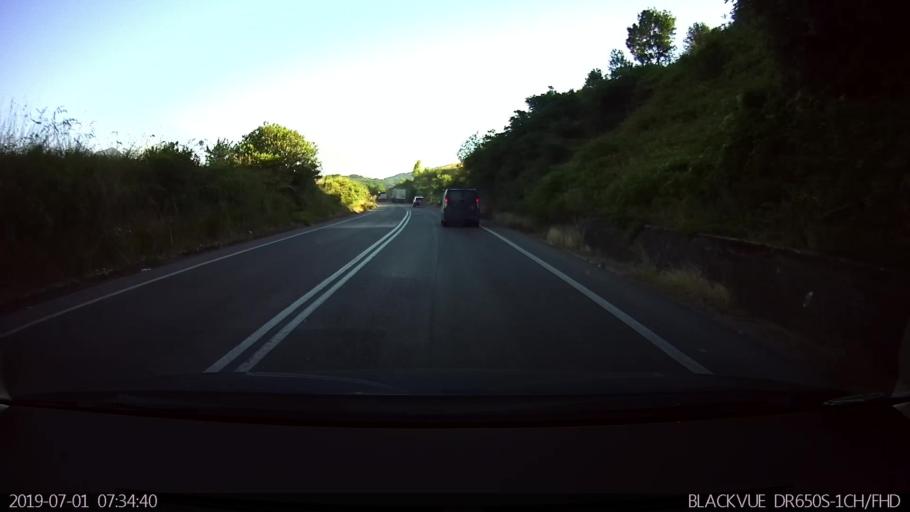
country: IT
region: Latium
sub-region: Provincia di Latina
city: Prossedi
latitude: 41.5178
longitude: 13.2728
